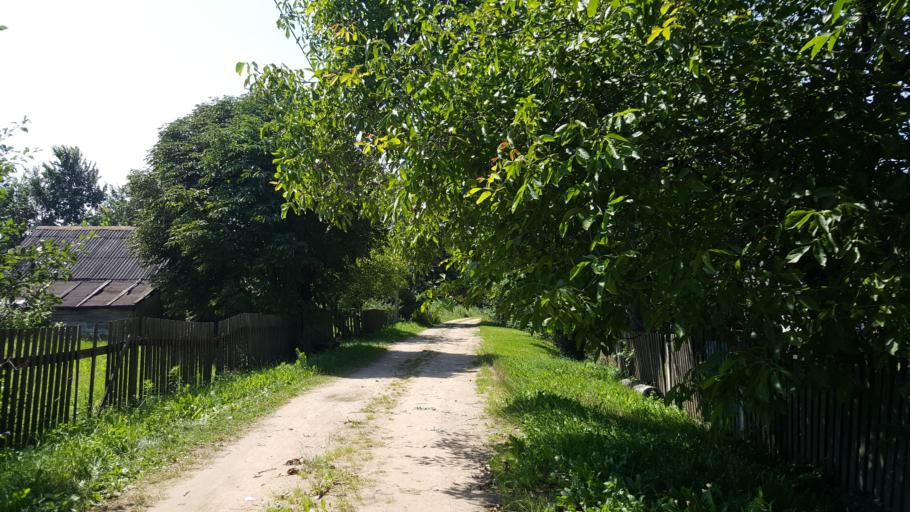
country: BY
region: Brest
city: Vysokaye
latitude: 52.3637
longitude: 23.5353
